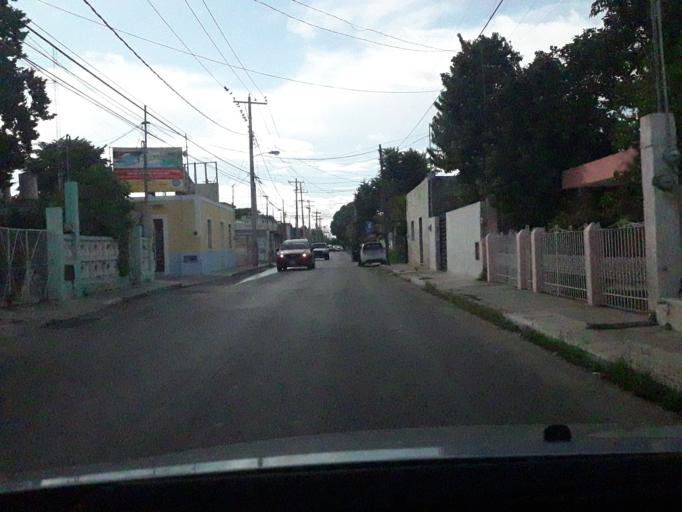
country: MX
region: Yucatan
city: Merida
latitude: 21.0122
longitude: -89.6353
